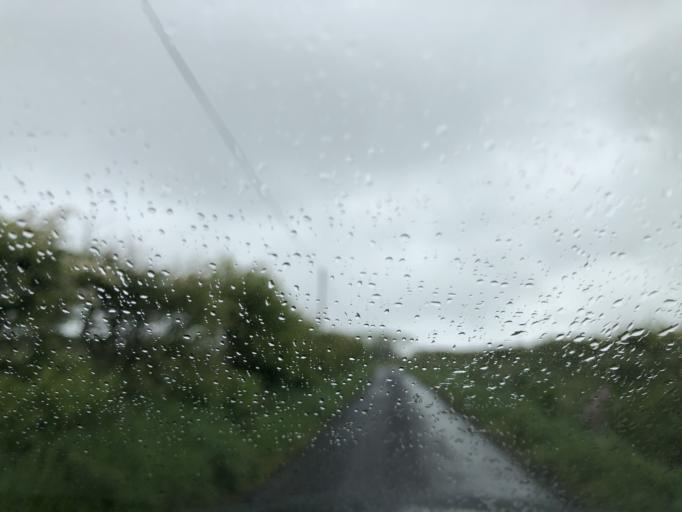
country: GB
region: Northern Ireland
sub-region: Moyle District
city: Ballycastle
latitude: 55.2096
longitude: -6.1616
